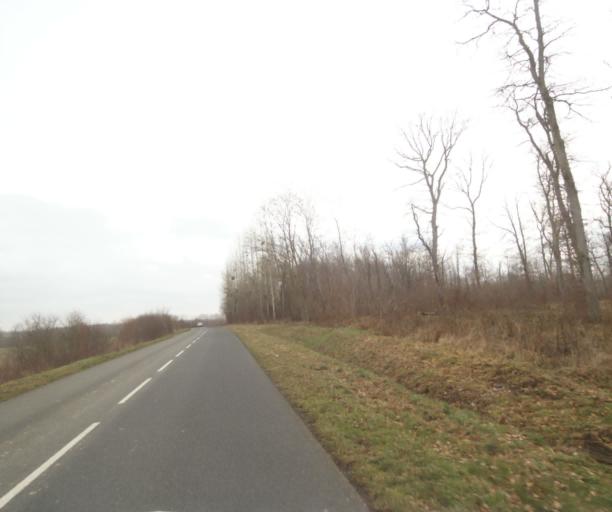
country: FR
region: Champagne-Ardenne
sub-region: Departement de la Marne
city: Pargny-sur-Saulx
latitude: 48.7406
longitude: 4.8664
